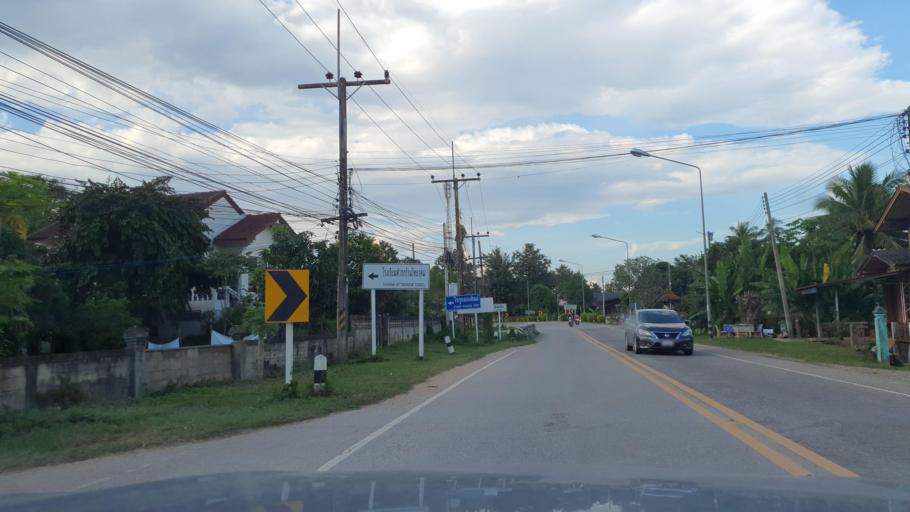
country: TH
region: Phayao
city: Phayao
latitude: 19.1314
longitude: 99.8414
